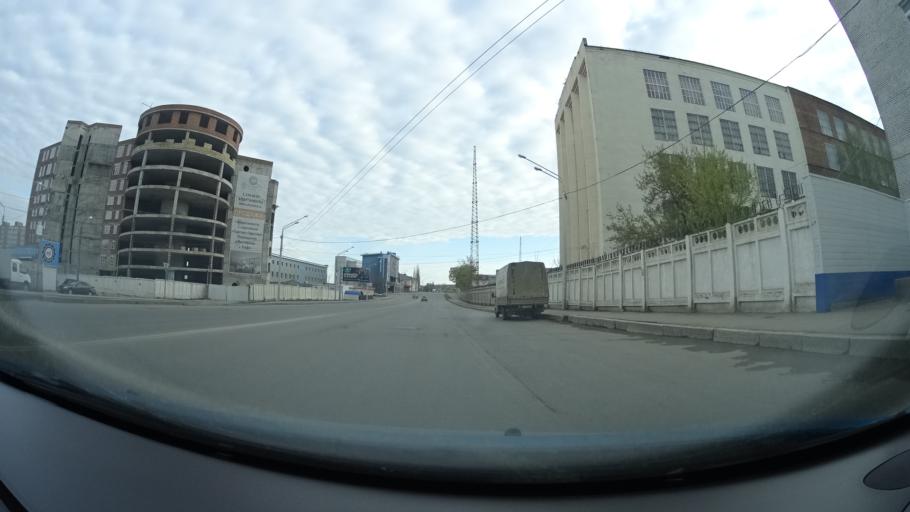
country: RU
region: Bashkortostan
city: Ufa
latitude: 54.7425
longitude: 55.9676
